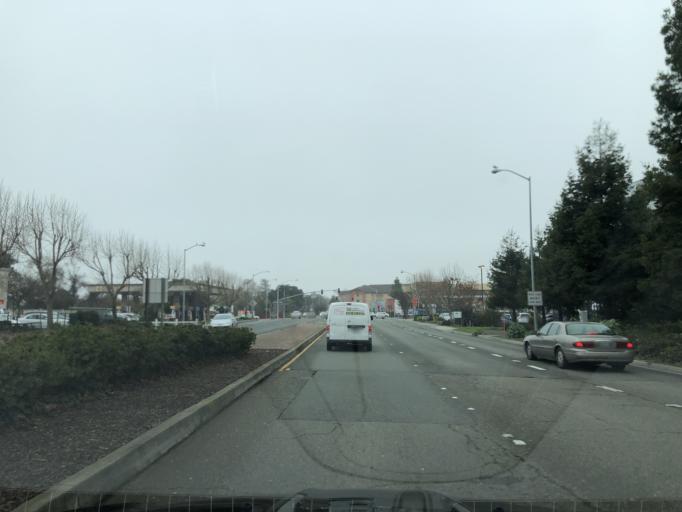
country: US
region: California
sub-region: Alameda County
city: Union City
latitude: 37.5984
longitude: -122.0647
